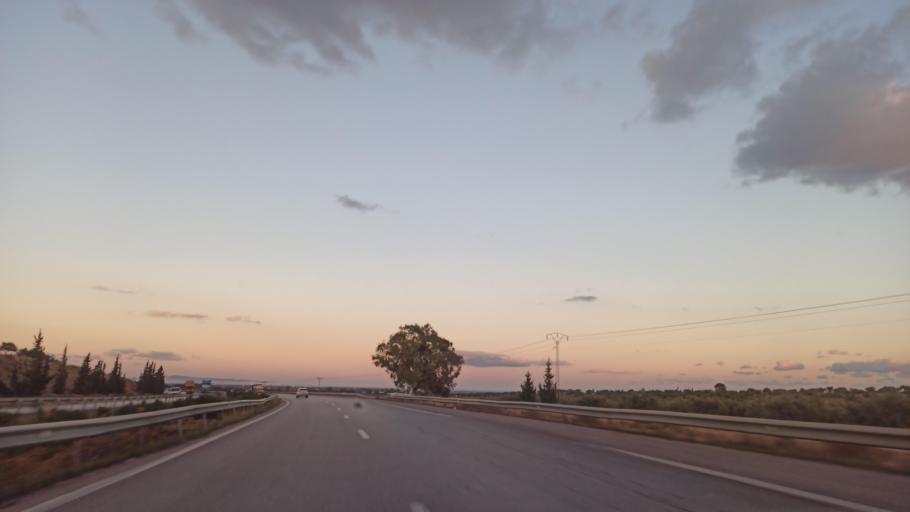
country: TN
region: Susah
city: Harqalah
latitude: 36.2398
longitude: 10.4197
